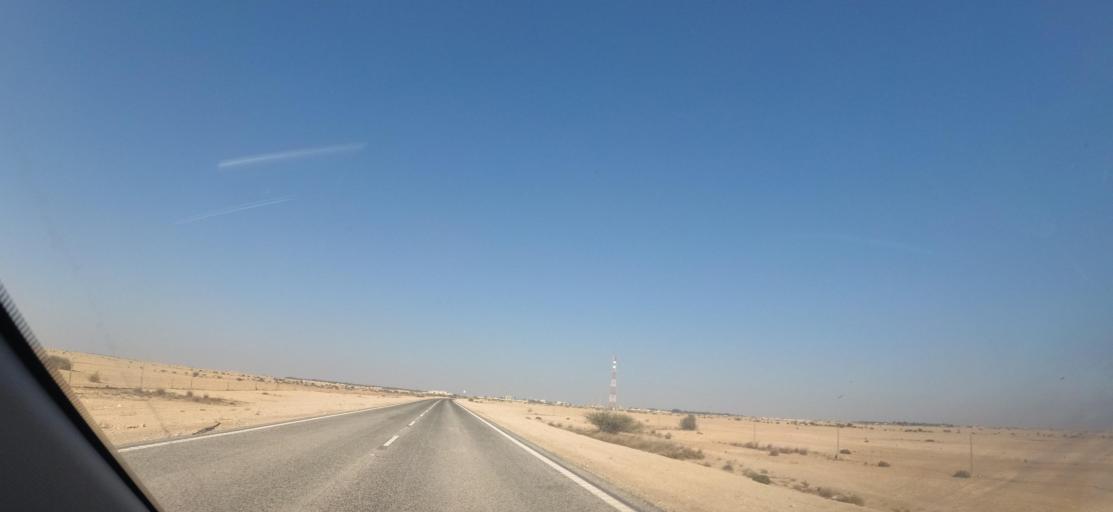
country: QA
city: Al Ghuwayriyah
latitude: 25.8120
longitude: 51.2300
